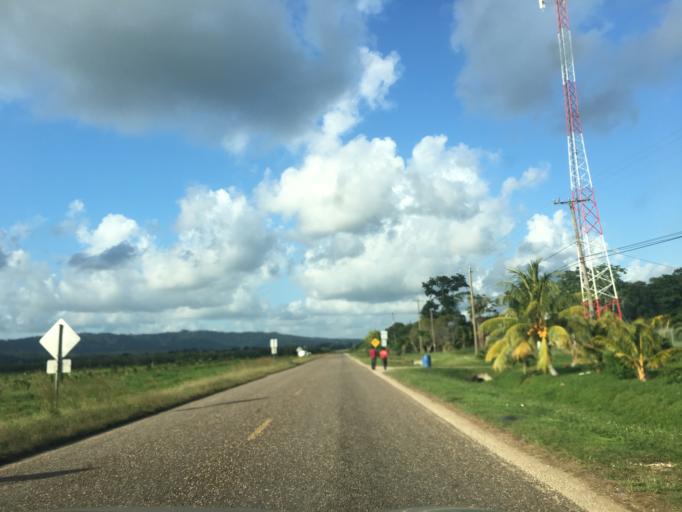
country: BZ
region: Stann Creek
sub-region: Dangriga
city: Dangriga
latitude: 16.8004
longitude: -88.3799
